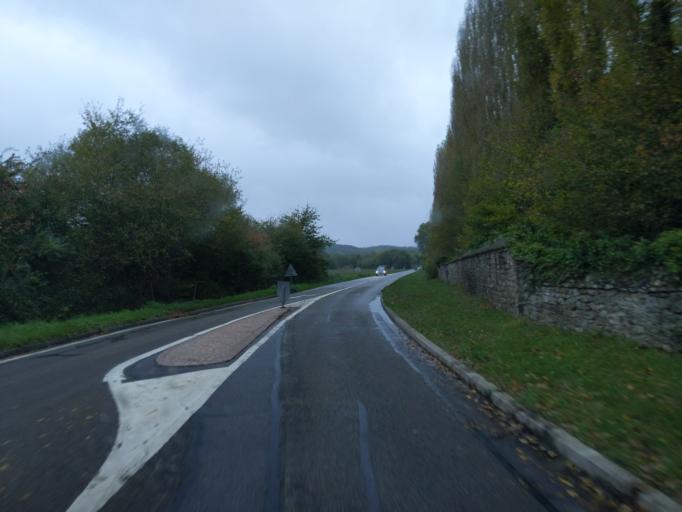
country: FR
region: Ile-de-France
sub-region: Departement des Yvelines
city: Dampierre-en-Yvelines
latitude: 48.6908
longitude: 1.9746
